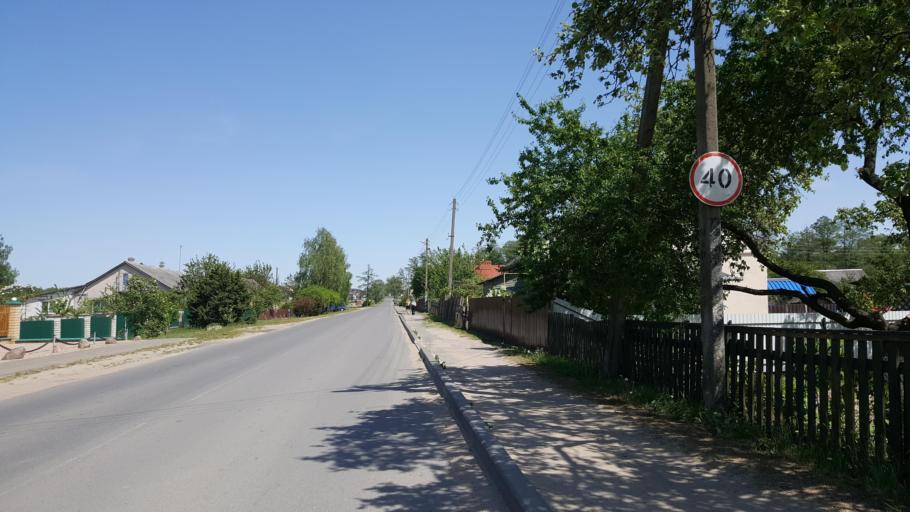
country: BY
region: Brest
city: Brest
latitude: 52.1587
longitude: 23.6507
